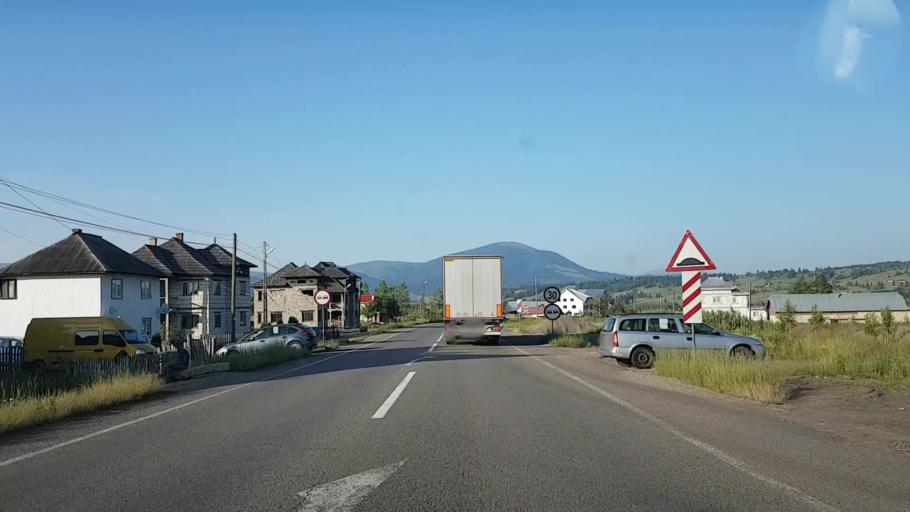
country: RO
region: Suceava
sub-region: Comuna Poiana Stampei
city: Poiana Stampei
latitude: 47.3279
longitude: 25.1455
